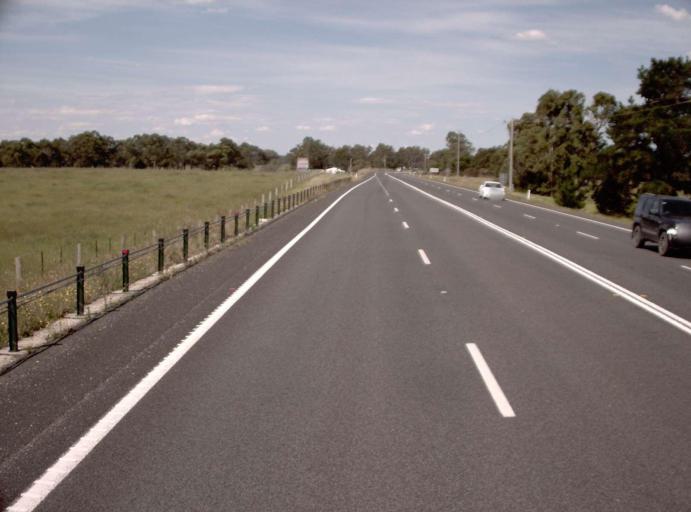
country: AU
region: Victoria
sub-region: East Gippsland
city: Lakes Entrance
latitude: -37.8207
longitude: 147.8094
